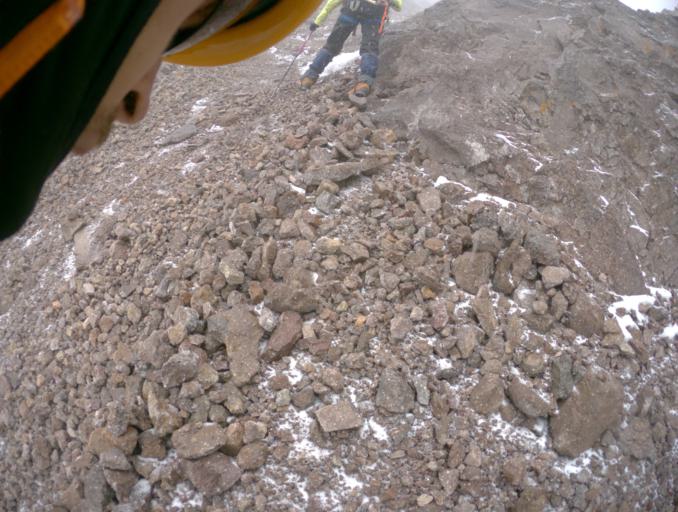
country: RU
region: Kabardino-Balkariya
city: Terskol
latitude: 43.3796
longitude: 42.4072
